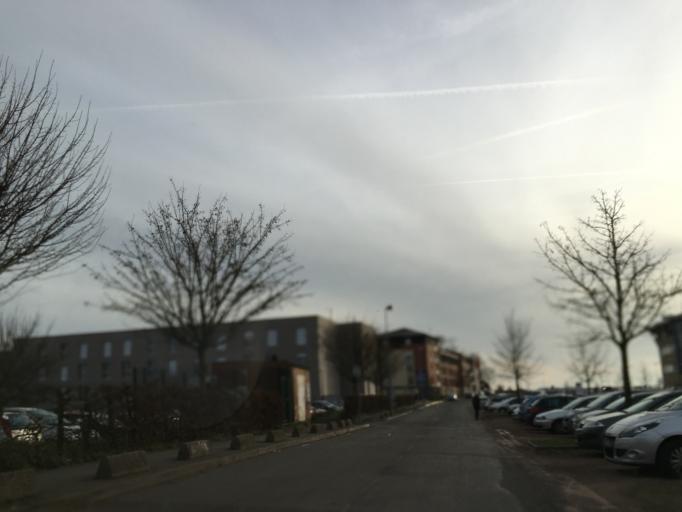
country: FR
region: Nord-Pas-de-Calais
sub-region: Departement du Pas-de-Calais
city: Saint-Laurent-Blangy
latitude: 50.2826
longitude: 2.7965
